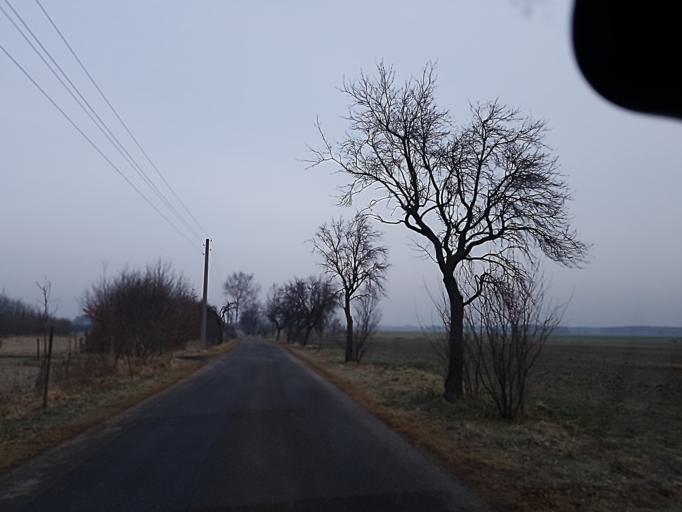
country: DE
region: Brandenburg
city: Ruckersdorf
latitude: 51.5673
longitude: 13.5452
